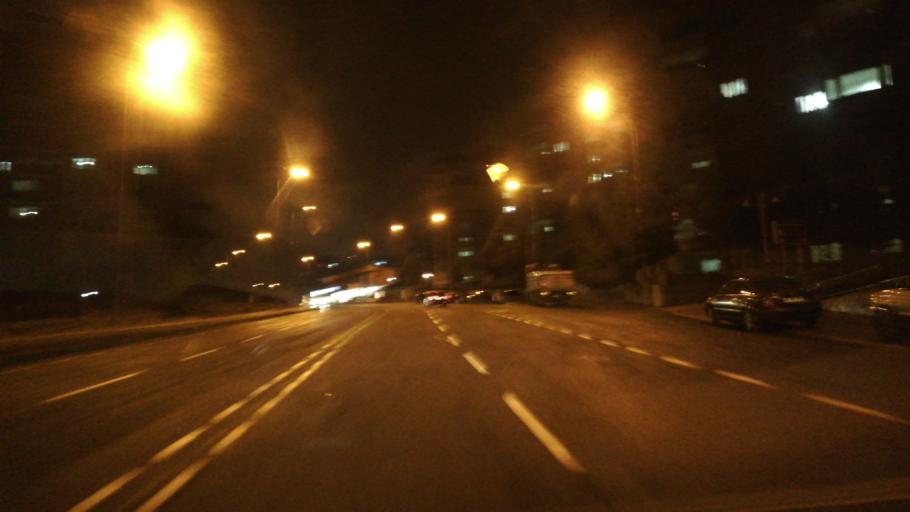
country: TR
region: Kahramanmaras
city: Kahramanmaras
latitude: 37.5764
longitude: 36.8550
